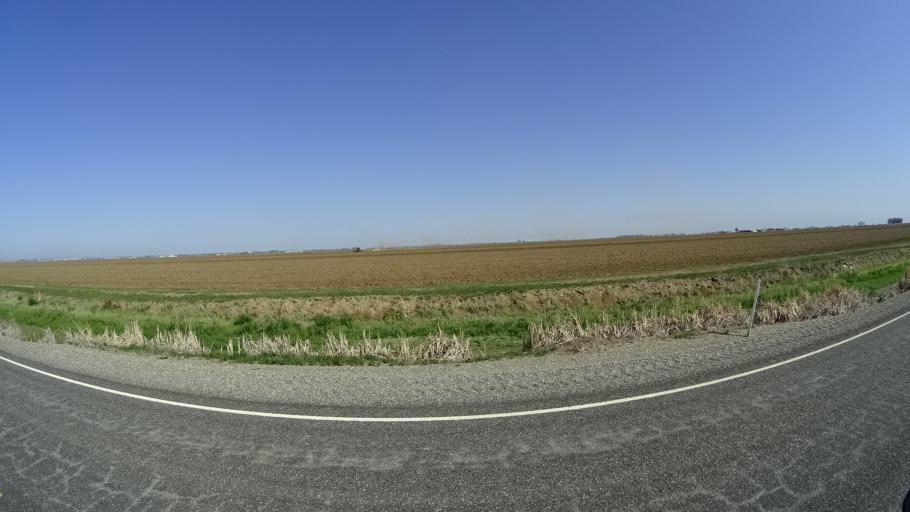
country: US
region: California
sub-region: Glenn County
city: Willows
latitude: 39.4656
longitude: -122.1625
